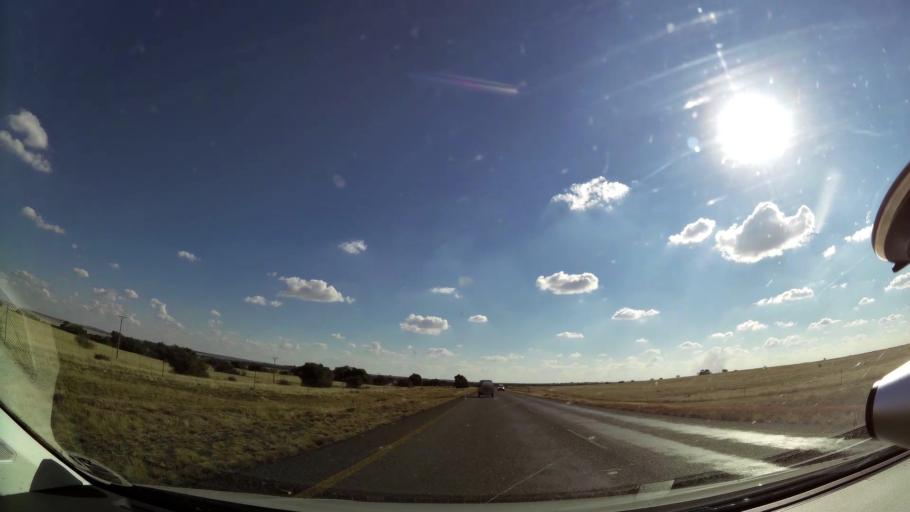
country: ZA
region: Northern Cape
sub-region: Frances Baard District Municipality
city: Kimberley
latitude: -28.8162
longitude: 24.8293
